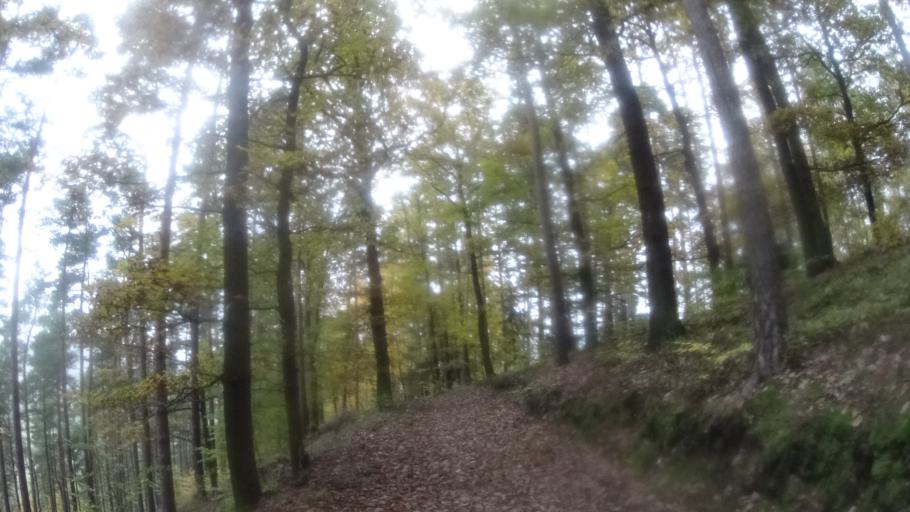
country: DE
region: Thuringia
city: Grosseutersdorf
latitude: 50.7791
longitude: 11.5652
